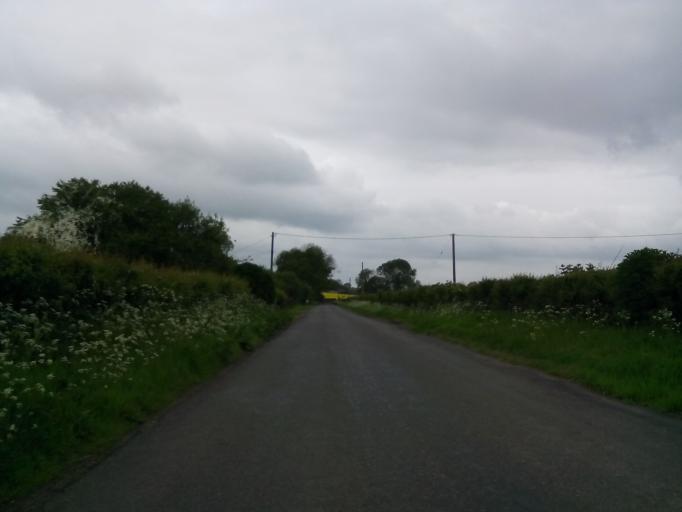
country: GB
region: England
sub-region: Northamptonshire
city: Oundle
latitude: 52.5162
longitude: -0.5326
